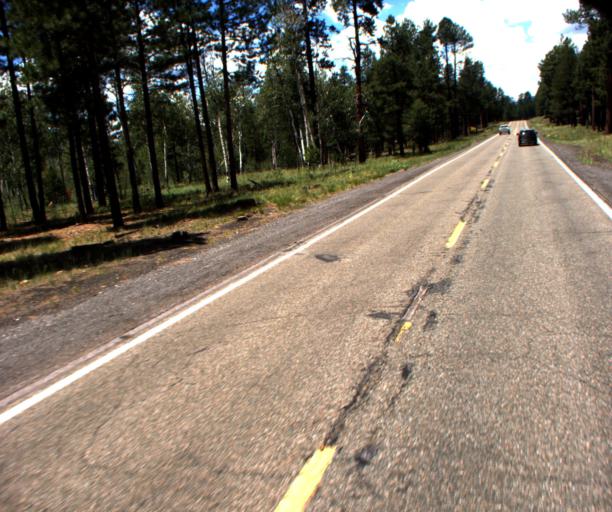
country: US
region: Arizona
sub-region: Coconino County
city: Flagstaff
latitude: 35.3288
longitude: -111.7771
